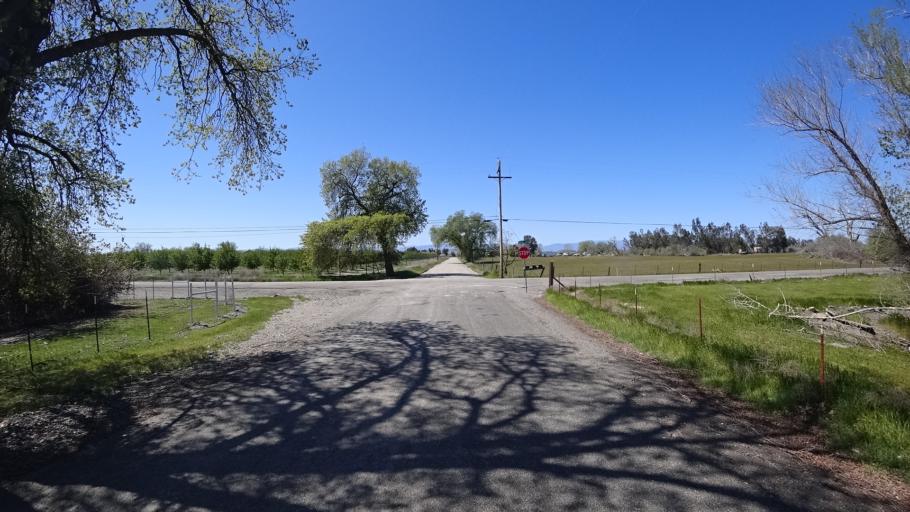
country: US
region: California
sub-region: Glenn County
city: Orland
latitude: 39.7768
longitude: -122.2473
